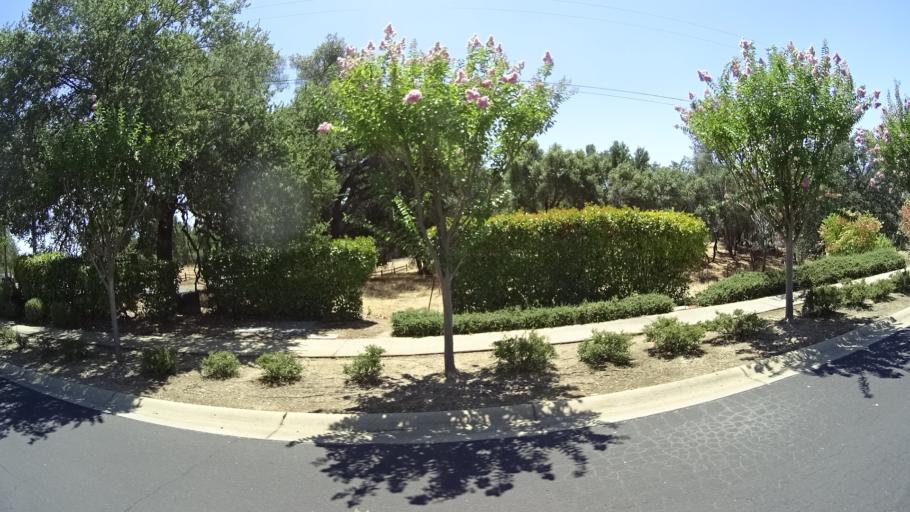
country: US
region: California
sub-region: Calaveras County
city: Angels Camp
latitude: 38.0620
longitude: -120.5545
